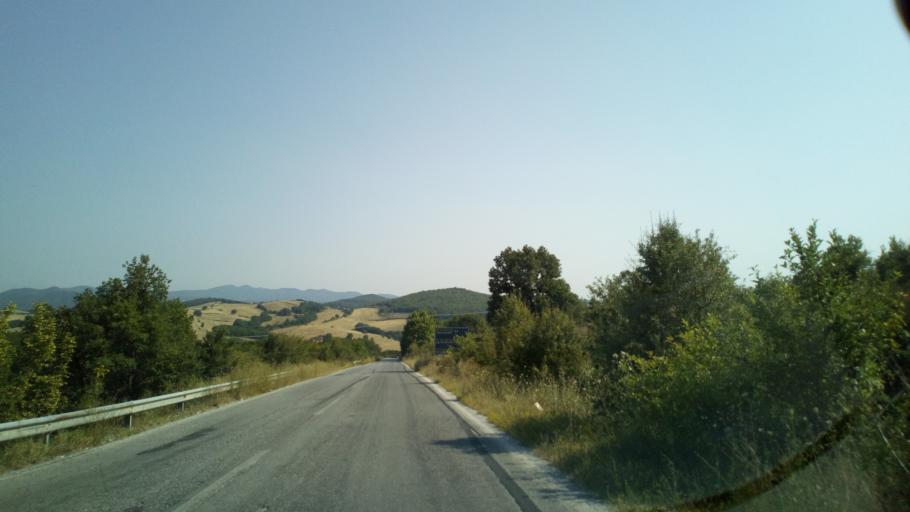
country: GR
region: Central Macedonia
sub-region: Nomos Chalkidikis
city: Polygyros
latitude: 40.4846
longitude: 23.4005
